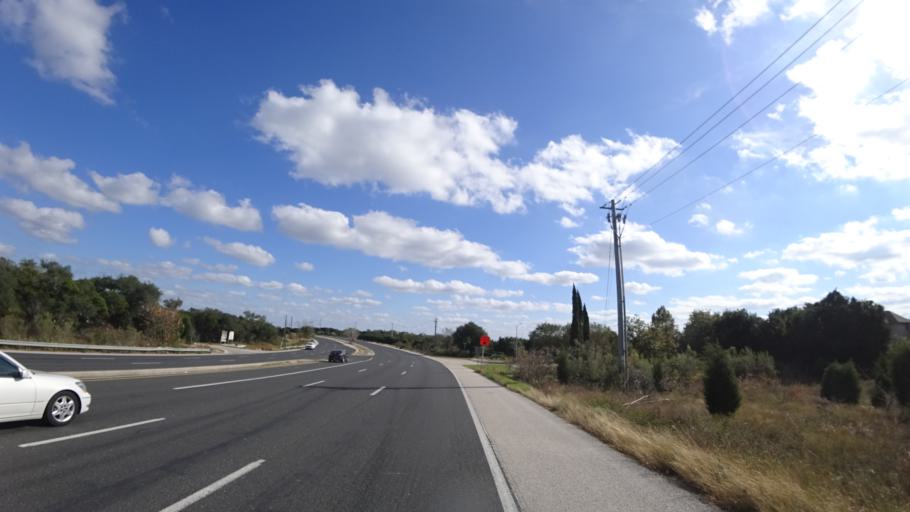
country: US
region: Texas
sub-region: Travis County
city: Barton Creek
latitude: 30.2579
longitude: -97.8825
